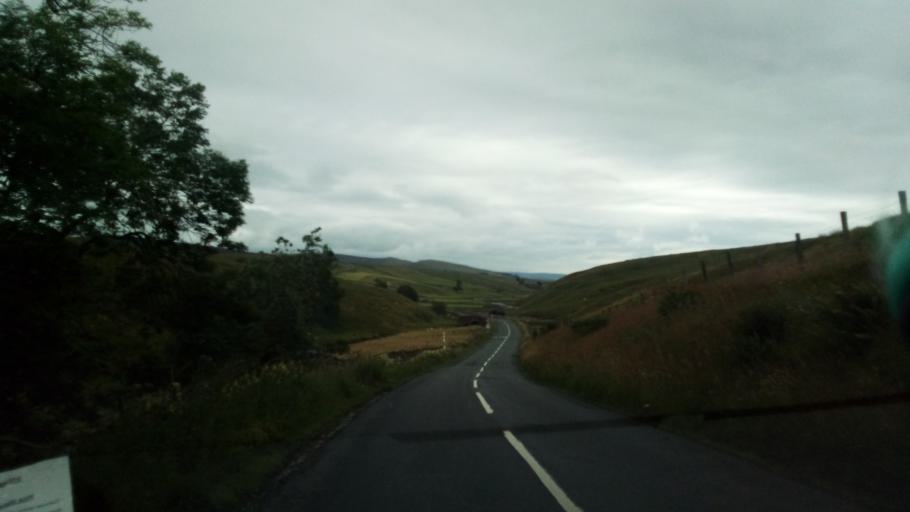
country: GB
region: England
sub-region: County Durham
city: Holwick
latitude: 54.5803
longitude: -2.2115
